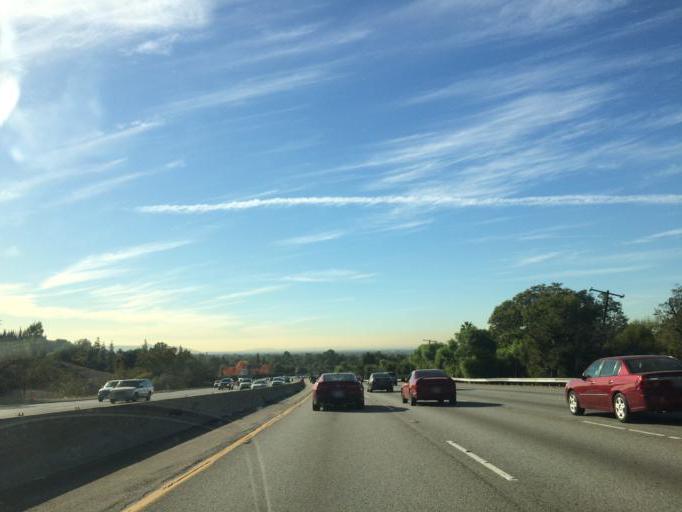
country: US
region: California
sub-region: Los Angeles County
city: Charter Oak
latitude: 34.0685
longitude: -117.8529
